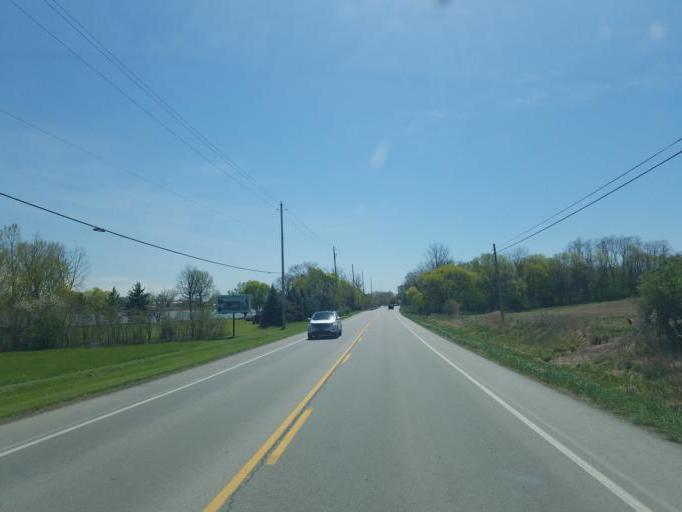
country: US
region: Ohio
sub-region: Ottawa County
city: Port Clinton
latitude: 41.5313
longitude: -82.8569
